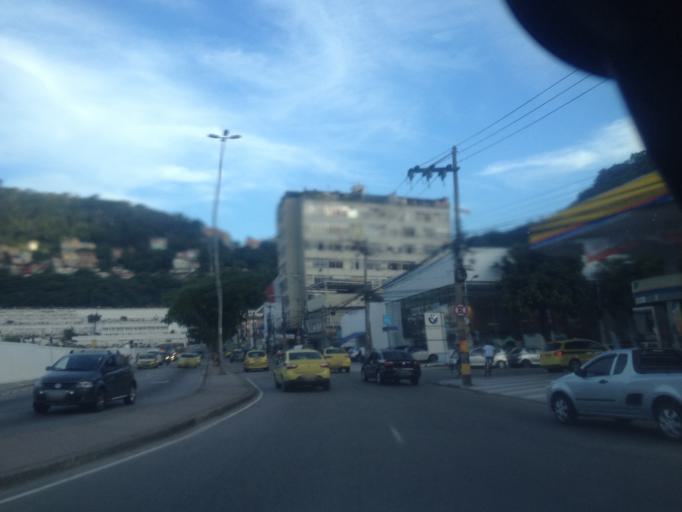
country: BR
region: Rio de Janeiro
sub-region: Rio De Janeiro
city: Rio de Janeiro
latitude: -22.9581
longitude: -43.1914
